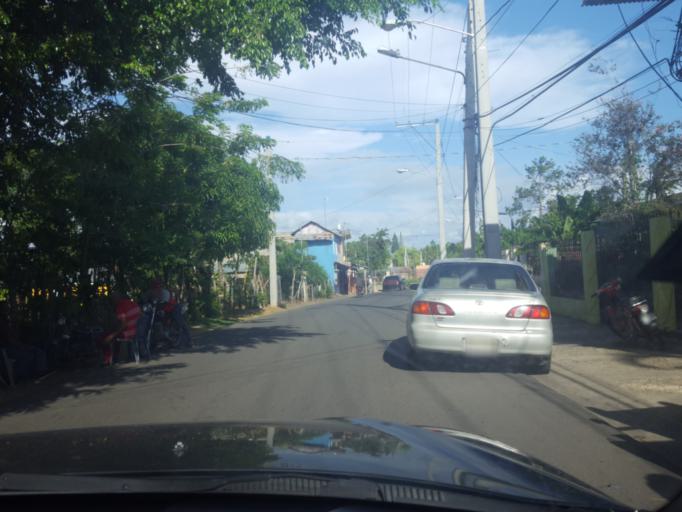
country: DO
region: La Vega
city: Rio Verde Arriba
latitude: 19.3455
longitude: -70.6216
